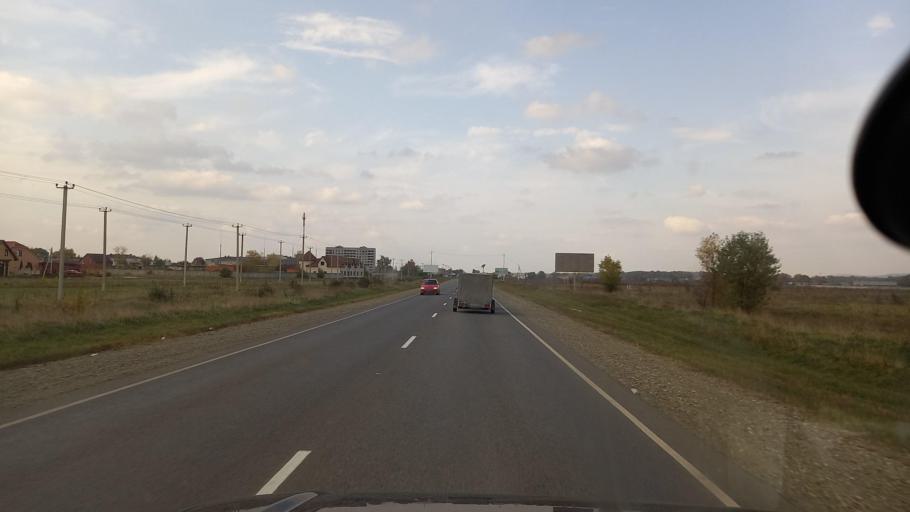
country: RU
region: Krasnodarskiy
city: Mostovskoy
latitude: 44.3867
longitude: 40.8177
